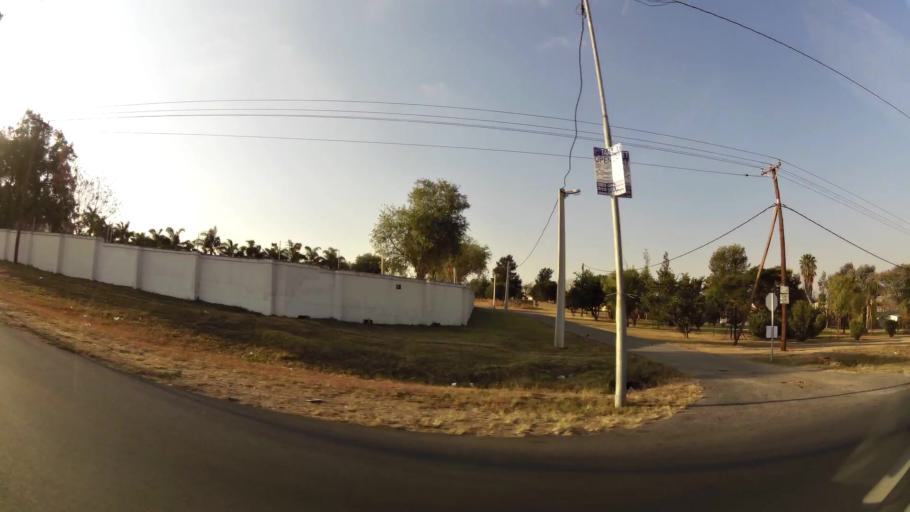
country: ZA
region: Gauteng
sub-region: City of Johannesburg Metropolitan Municipality
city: Midrand
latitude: -26.0242
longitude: 28.1561
